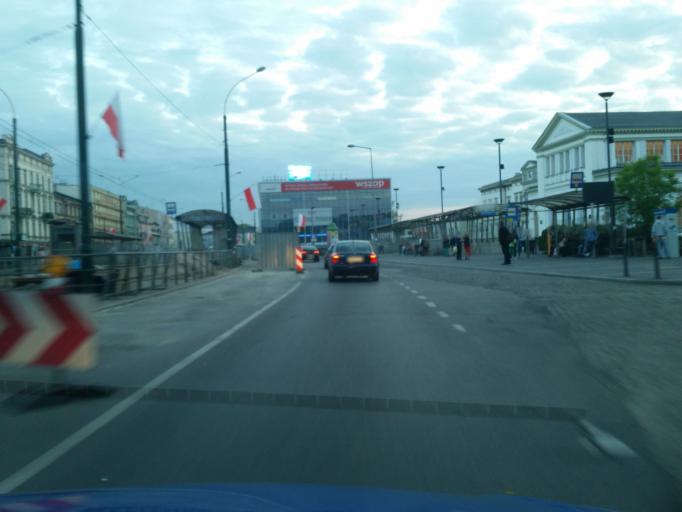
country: PL
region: Silesian Voivodeship
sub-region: Sosnowiec
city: Sosnowiec
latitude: 50.2787
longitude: 19.1277
